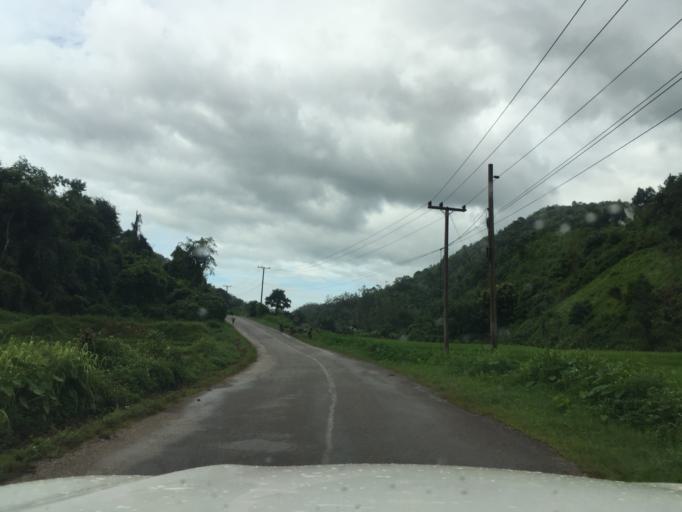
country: LA
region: Oudomxai
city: Muang La
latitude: 20.8187
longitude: 102.0934
